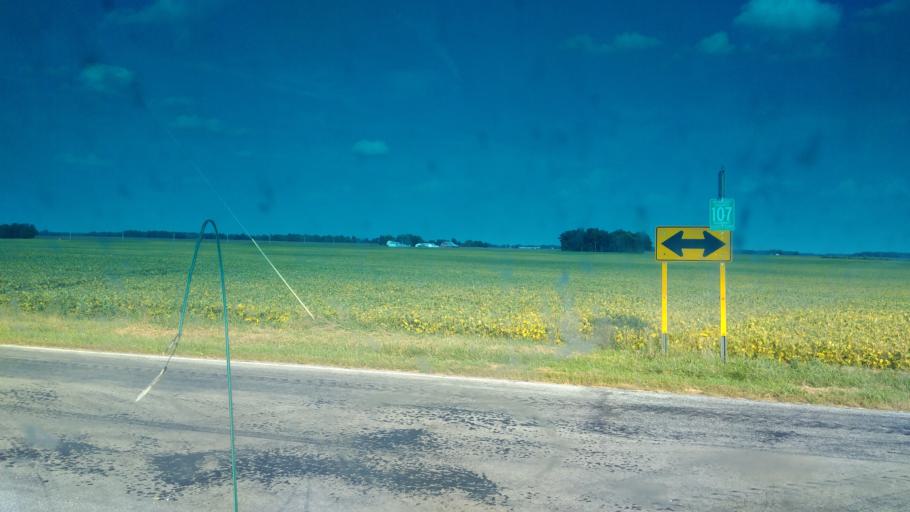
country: US
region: Ohio
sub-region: Wyandot County
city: Carey
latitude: 40.9237
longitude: -83.3046
